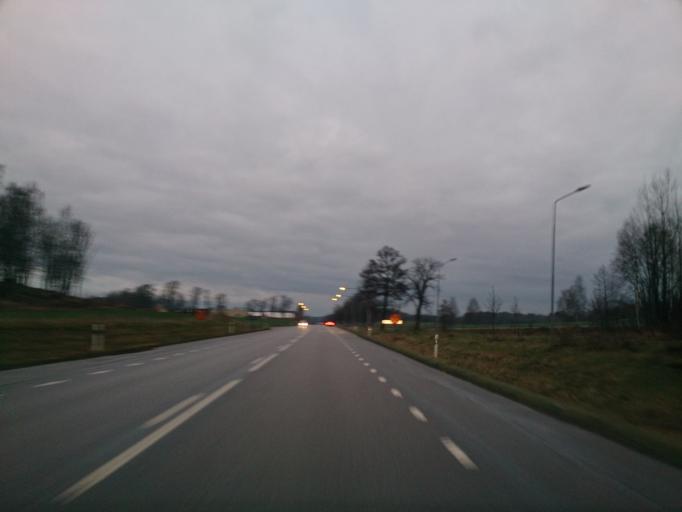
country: SE
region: OEstergoetland
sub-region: Atvidabergs Kommun
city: Atvidaberg
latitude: 58.2234
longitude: 15.9700
